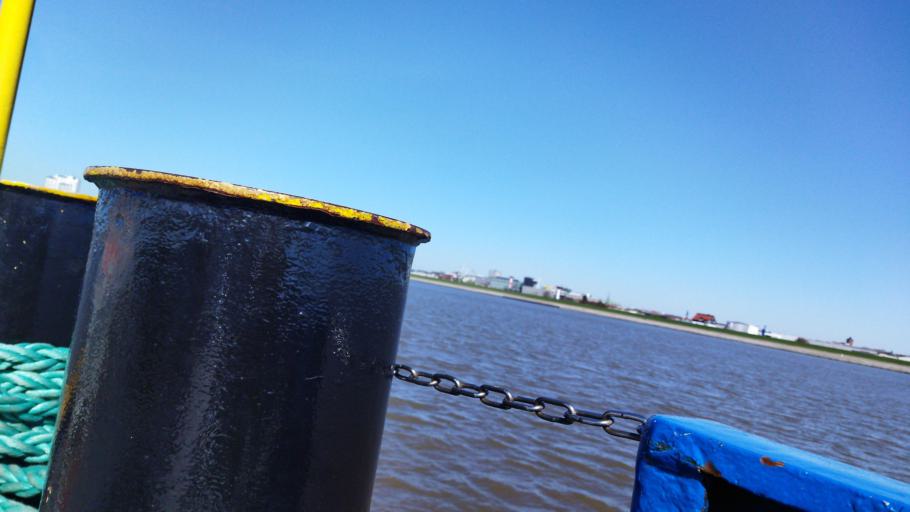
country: DE
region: Bremen
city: Bremerhaven
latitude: 53.5291
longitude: 8.5672
